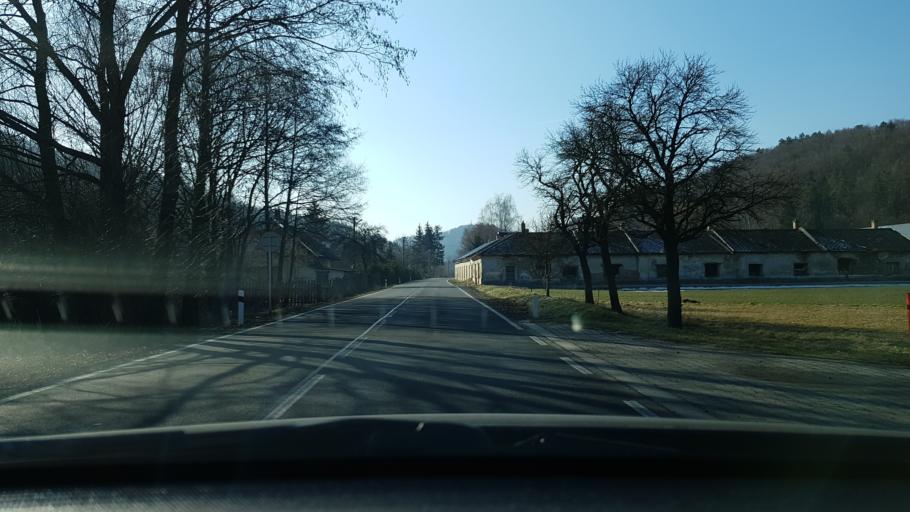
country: CZ
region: Olomoucky
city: Dolni Bohdikov
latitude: 49.9976
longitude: 16.8943
